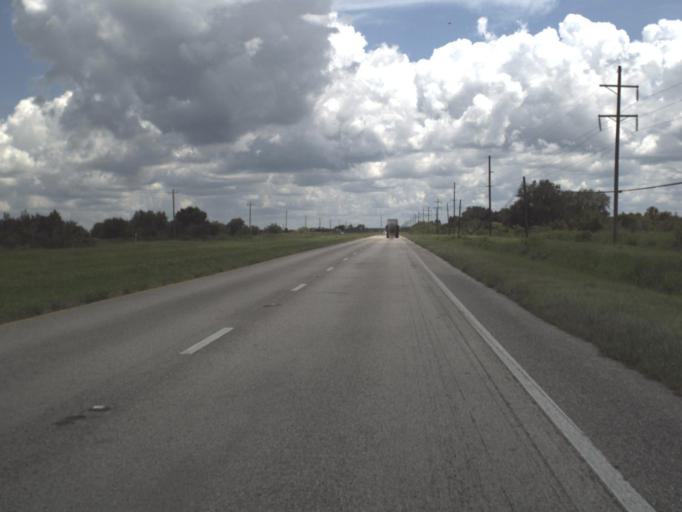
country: US
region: Florida
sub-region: Polk County
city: Babson Park
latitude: 27.8505
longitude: -81.3659
